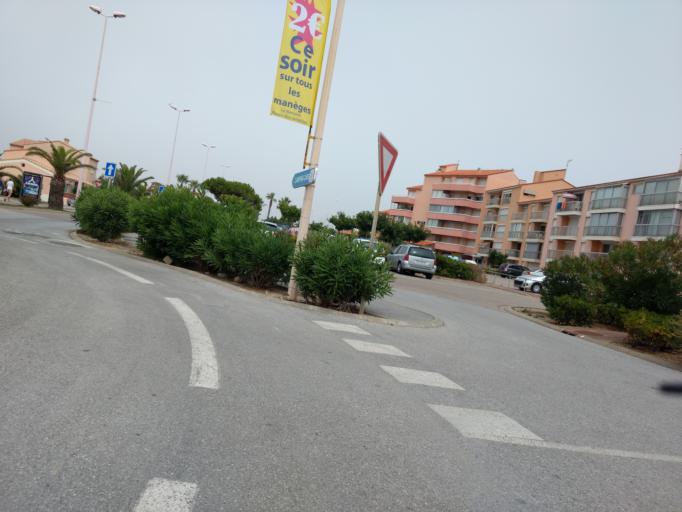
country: FR
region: Languedoc-Roussillon
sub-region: Departement des Pyrenees-Orientales
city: Le Barcares
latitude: 42.7950
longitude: 3.0366
